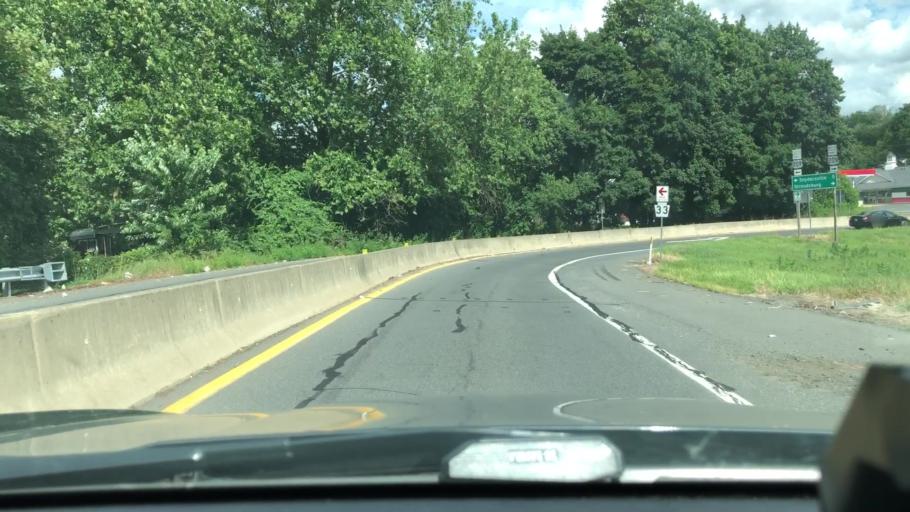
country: US
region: Pennsylvania
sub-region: Monroe County
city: Arlington Heights
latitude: 40.9814
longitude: -75.2140
